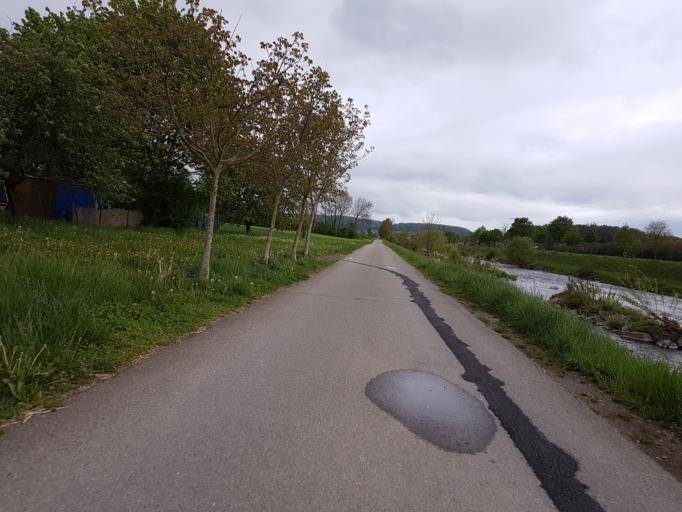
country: DE
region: Baden-Wuerttemberg
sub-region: Freiburg Region
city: Wutoschingen
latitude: 47.6521
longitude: 8.3576
